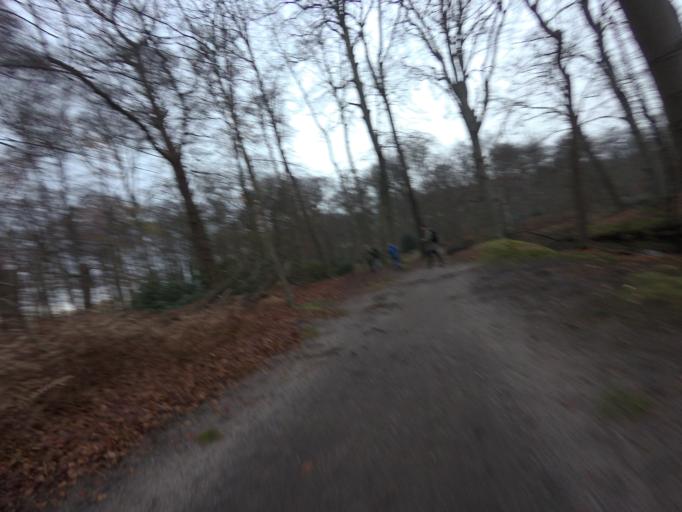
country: NL
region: North Holland
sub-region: Gemeente Wijdemeren
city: Kortenhoef
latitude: 52.2426
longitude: 5.1340
